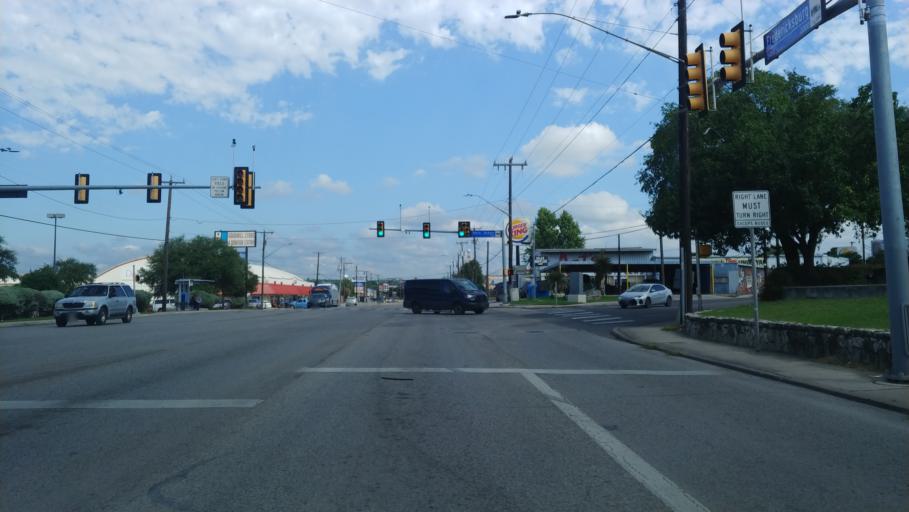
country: US
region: Texas
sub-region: Bexar County
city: Balcones Heights
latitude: 29.4733
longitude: -98.5347
